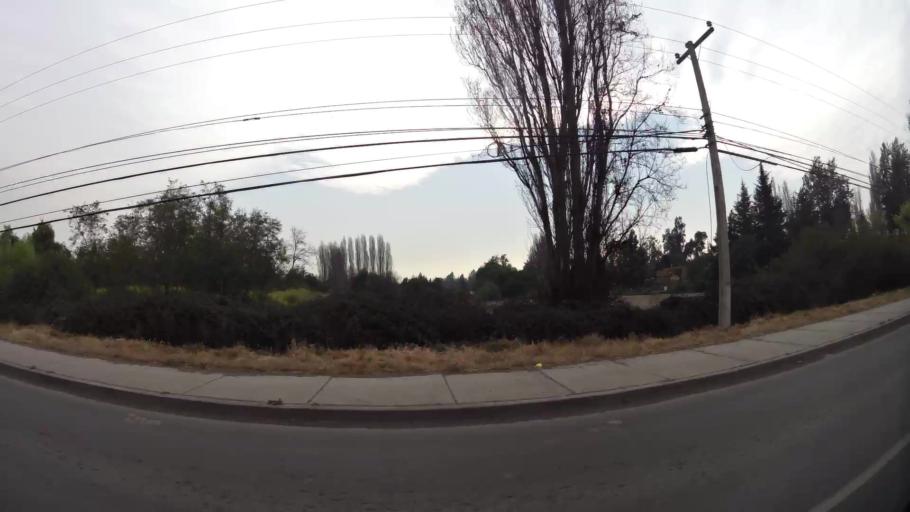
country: CL
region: Santiago Metropolitan
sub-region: Provincia de Chacabuco
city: Chicureo Abajo
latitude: -33.2674
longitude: -70.7001
